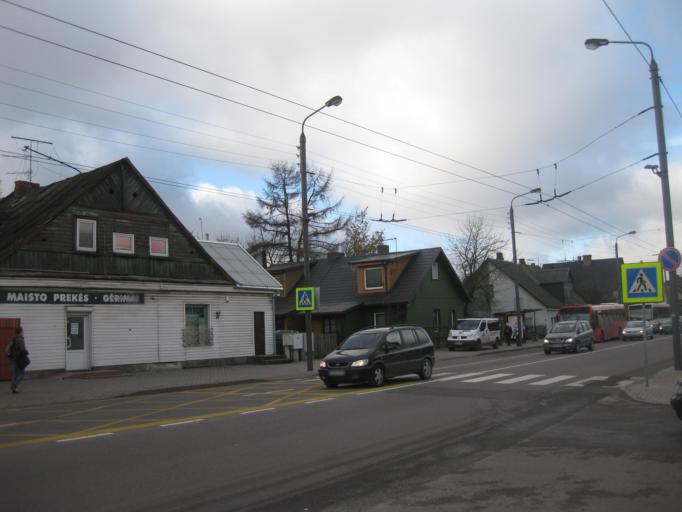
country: LT
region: Kauno apskritis
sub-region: Kaunas
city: Kaunas
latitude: 54.9049
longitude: 23.8864
